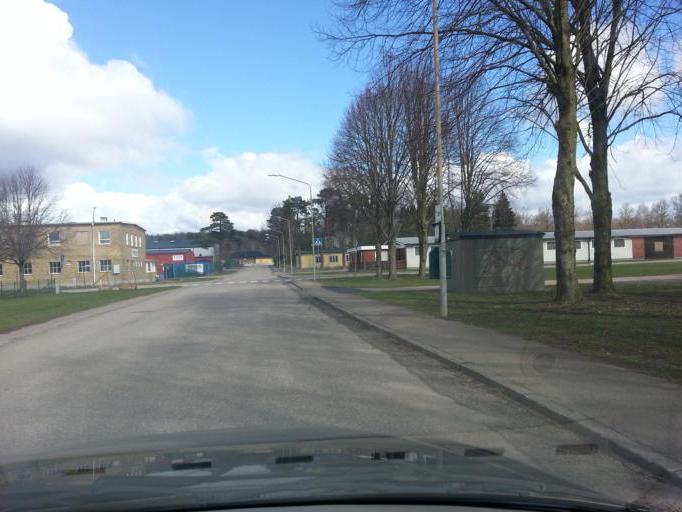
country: SE
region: Skane
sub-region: Perstorps Kommun
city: Perstorp
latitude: 56.1401
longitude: 13.3995
